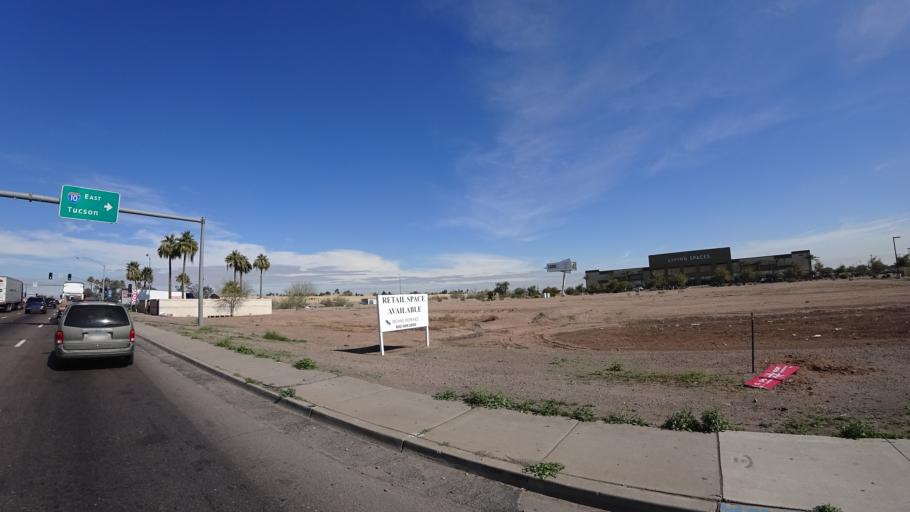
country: US
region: Arizona
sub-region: Maricopa County
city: Tolleson
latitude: 33.4612
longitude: -112.2033
